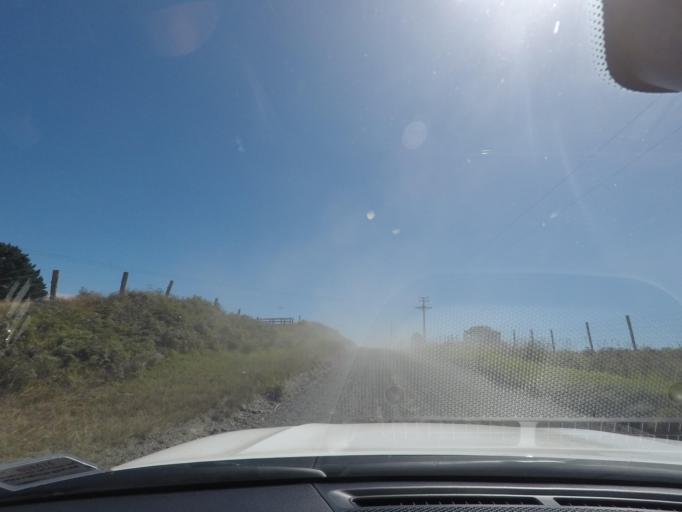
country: NZ
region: Auckland
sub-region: Auckland
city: Parakai
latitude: -36.5844
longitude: 174.2946
